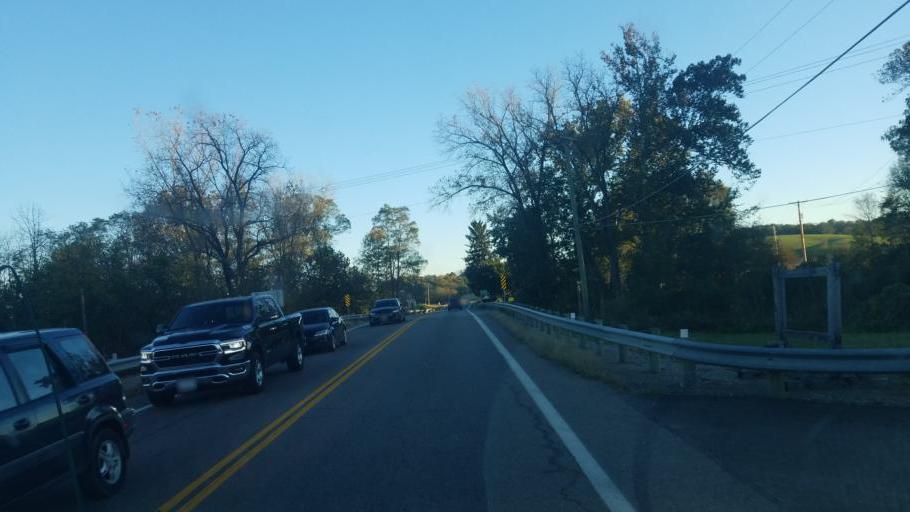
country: US
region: Ohio
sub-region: Licking County
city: Utica
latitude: 40.2286
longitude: -82.4516
